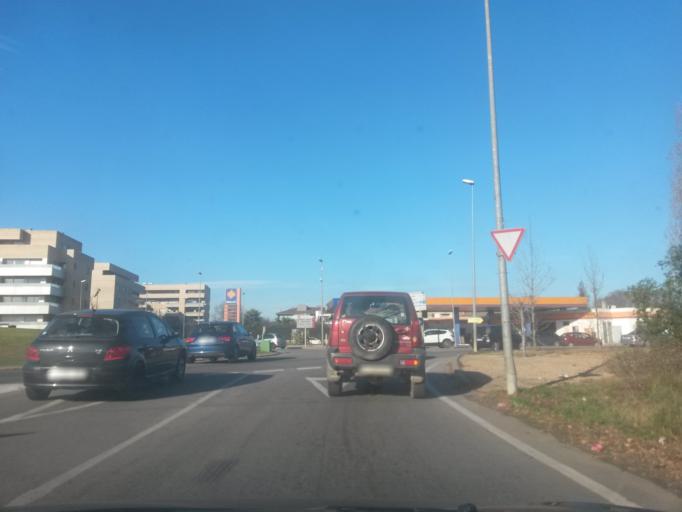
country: ES
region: Catalonia
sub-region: Provincia de Girona
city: Salt
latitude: 41.9667
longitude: 2.7880
